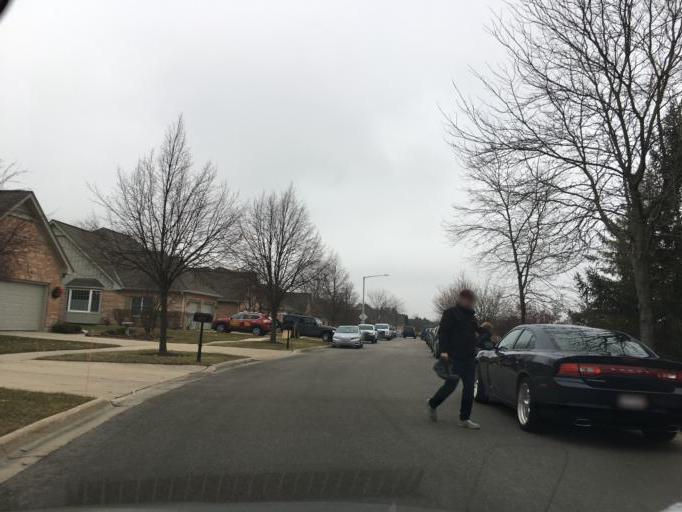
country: US
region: Illinois
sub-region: McHenry County
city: Lakewood
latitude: 42.2250
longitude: -88.3556
